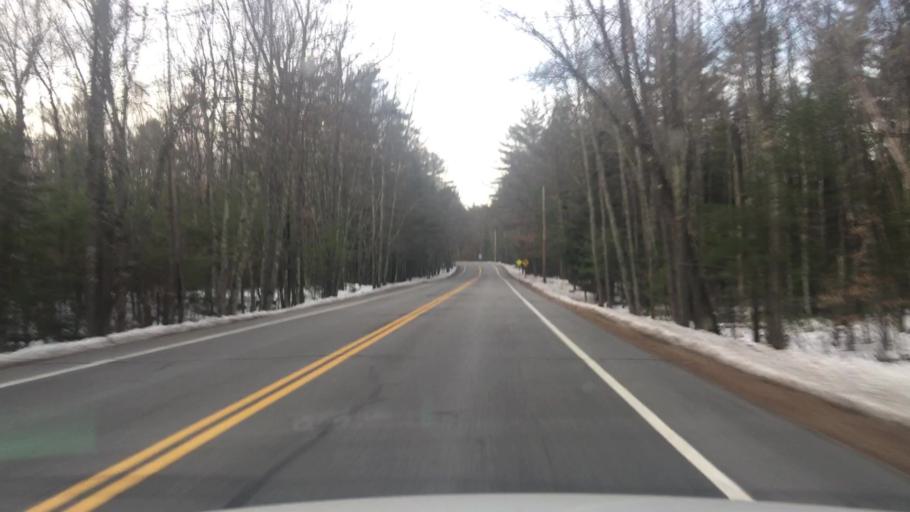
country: US
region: Maine
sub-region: York County
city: Dayton
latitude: 43.5633
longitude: -70.6209
